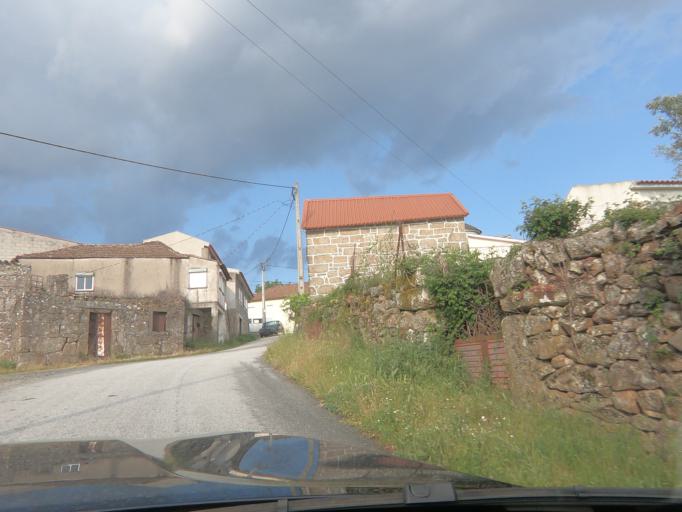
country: PT
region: Vila Real
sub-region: Vila Real
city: Vila Real
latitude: 41.3100
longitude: -7.6990
